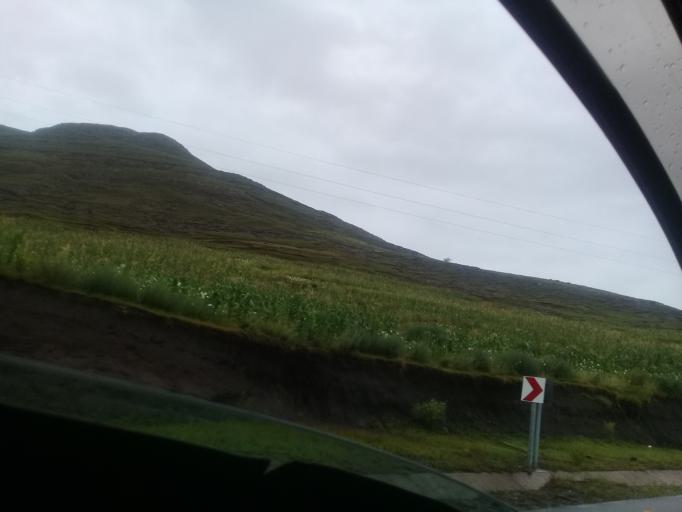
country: LS
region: Mokhotlong
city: Mokhotlong
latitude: -29.3312
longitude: 29.0300
